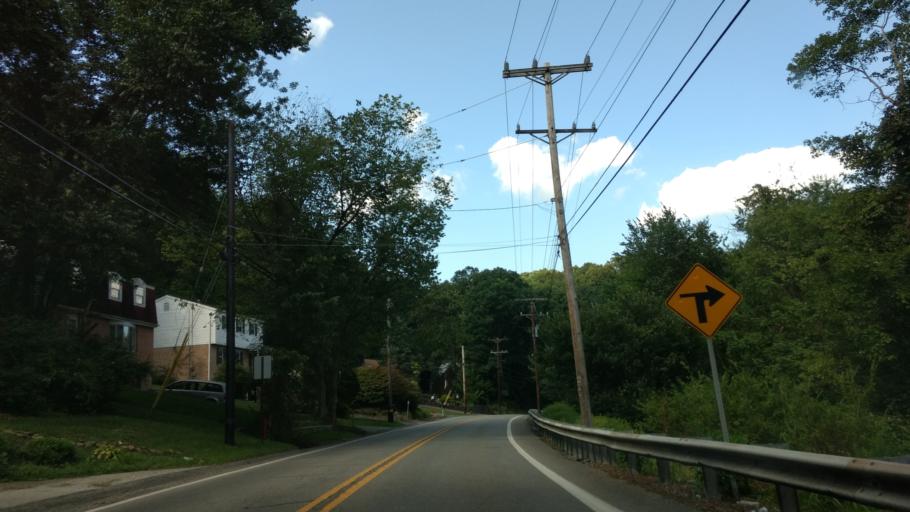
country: US
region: Pennsylvania
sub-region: Allegheny County
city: West View
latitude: 40.5427
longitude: -80.0450
